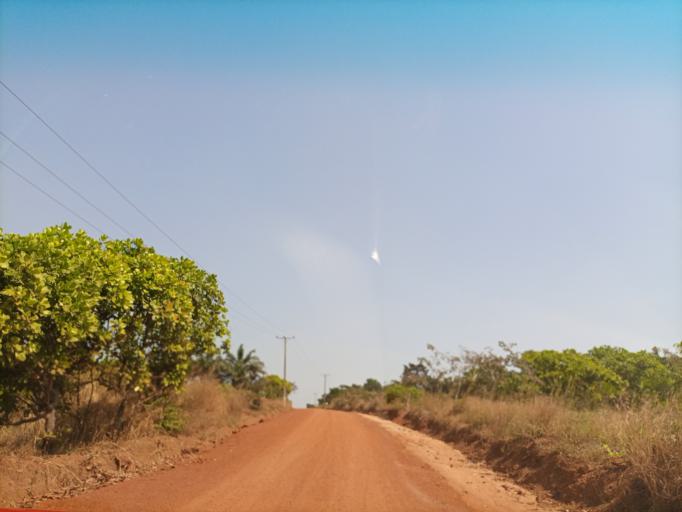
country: NG
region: Enugu
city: Nsukka
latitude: 6.7998
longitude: 7.3437
